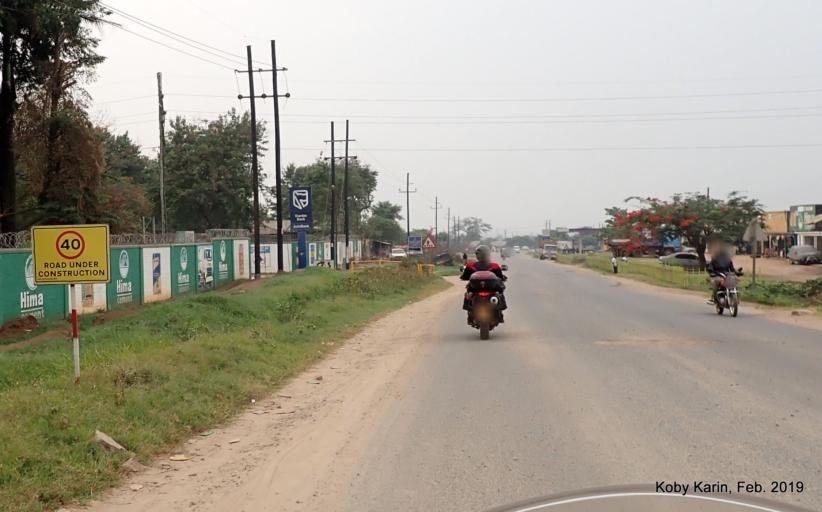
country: UG
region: Western Region
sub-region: Kasese District
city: Kasese
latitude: 0.2936
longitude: 30.1792
